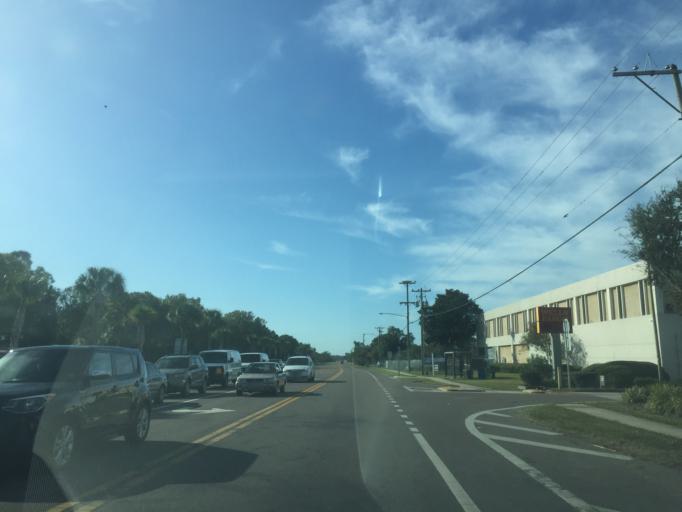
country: US
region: Florida
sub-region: Pinellas County
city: Dunedin
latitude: 28.0493
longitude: -82.7805
